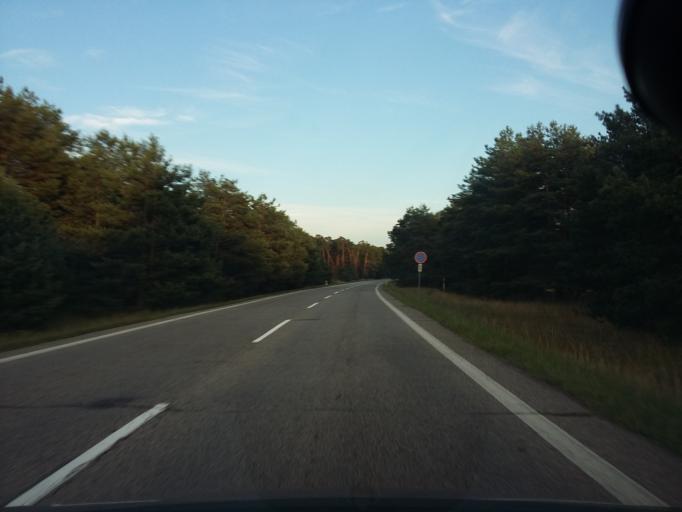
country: SK
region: Bratislavsky
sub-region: Okres Malacky
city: Malacky
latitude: 48.4061
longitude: 17.0789
